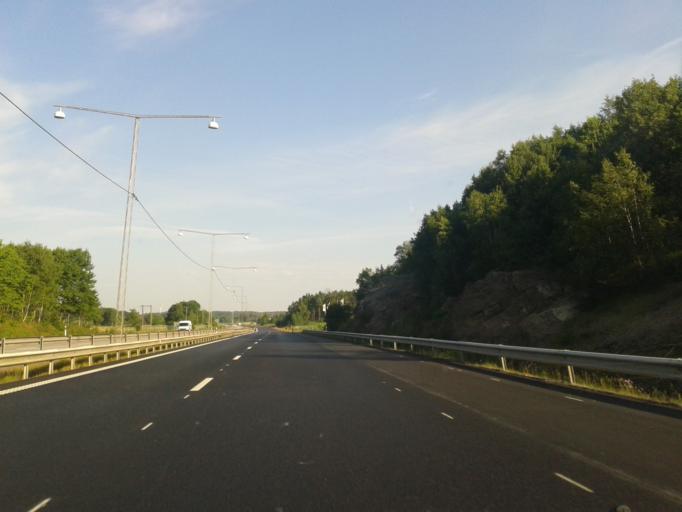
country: SE
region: Vaestra Goetaland
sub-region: Kungalvs Kommun
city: Kungalv
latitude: 57.8883
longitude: 11.9407
